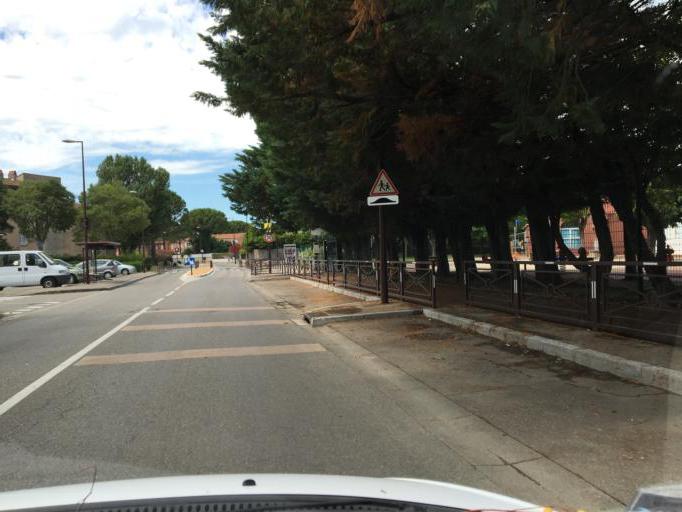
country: FR
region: Provence-Alpes-Cote d'Azur
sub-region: Departement du Vaucluse
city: Le Pontet
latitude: 43.9492
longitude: 4.8447
